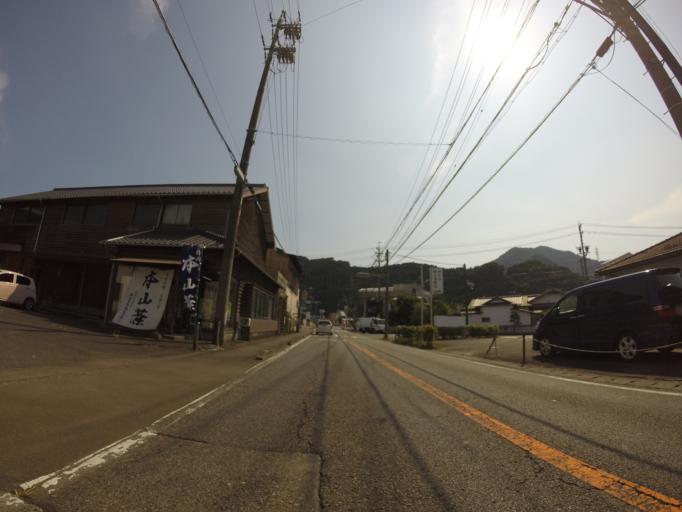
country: JP
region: Shizuoka
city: Shizuoka-shi
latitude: 35.0117
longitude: 138.3562
